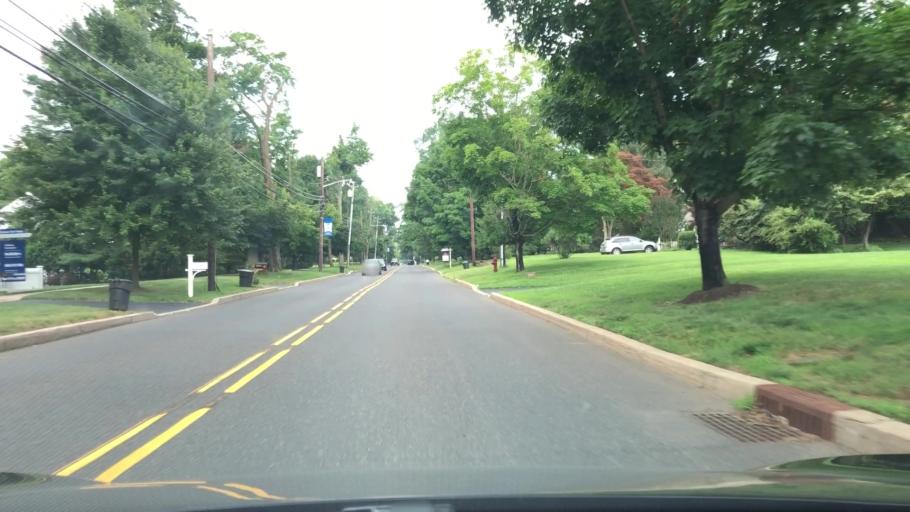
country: US
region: New Jersey
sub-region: Mercer County
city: Pennington
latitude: 40.3288
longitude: -74.7837
